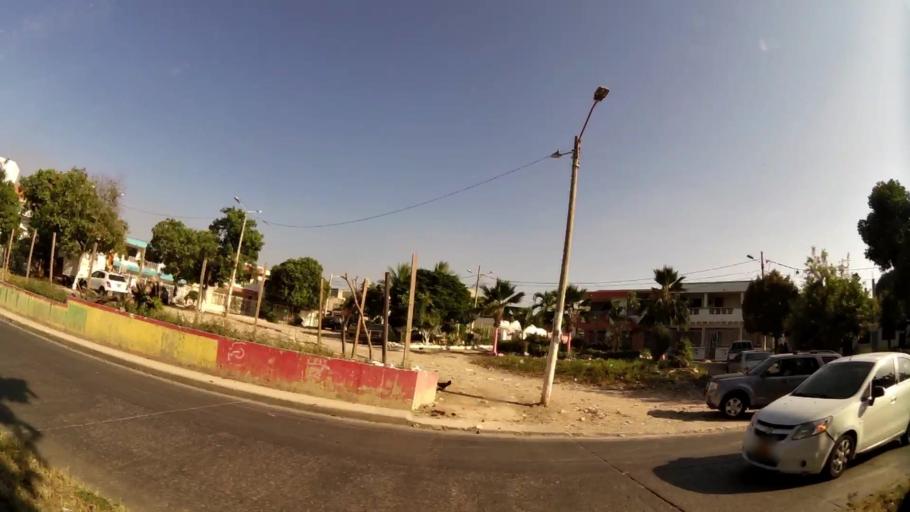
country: CO
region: Bolivar
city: Cartagena
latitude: 10.3829
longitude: -75.4866
